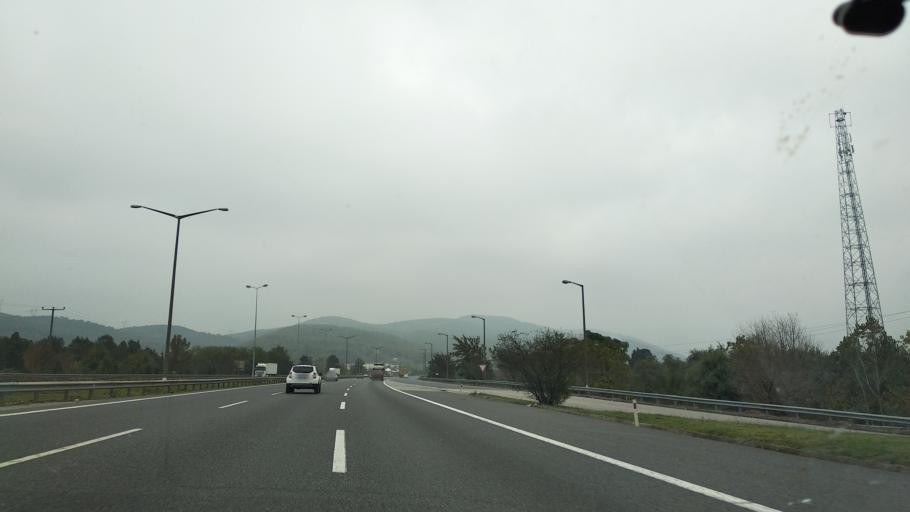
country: TR
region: Sakarya
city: Karadere
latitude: 40.8024
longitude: 30.8505
